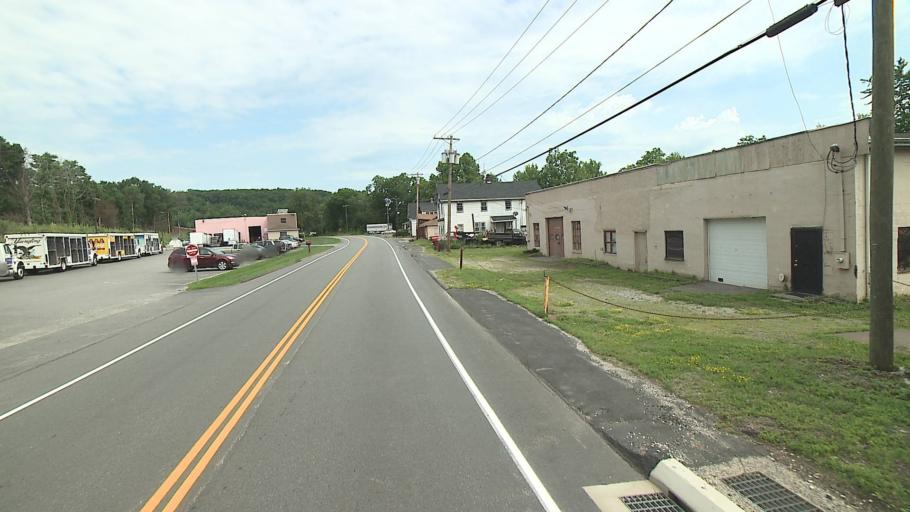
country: US
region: Connecticut
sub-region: Litchfield County
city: Torrington
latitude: 41.7717
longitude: -73.1190
